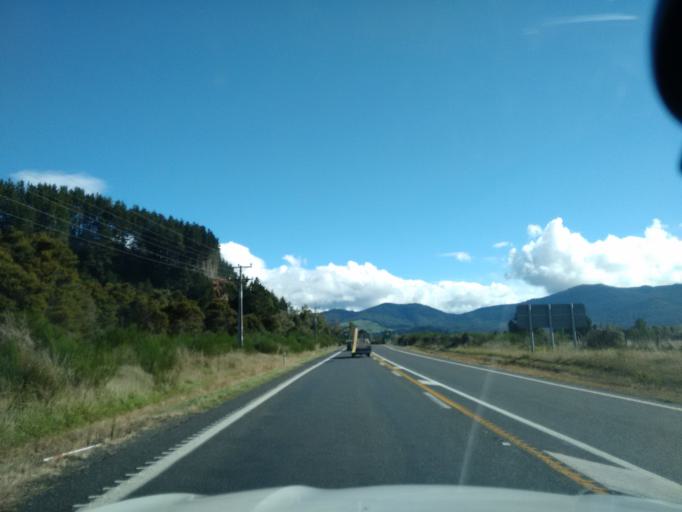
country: NZ
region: Waikato
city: Turangi
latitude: -38.9798
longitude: 175.8263
